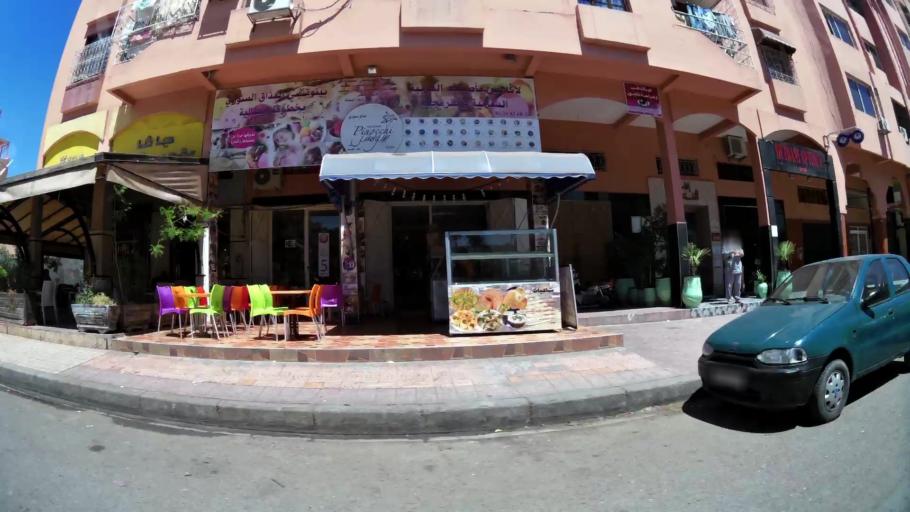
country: MA
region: Marrakech-Tensift-Al Haouz
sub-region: Marrakech
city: Marrakesh
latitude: 31.6347
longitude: -8.0562
